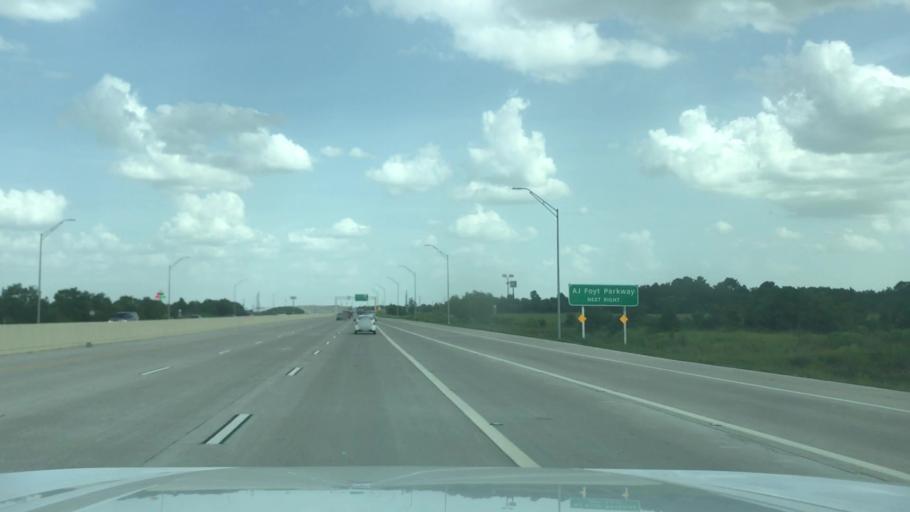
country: US
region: Texas
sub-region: Waller County
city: Waller
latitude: 30.0670
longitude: -95.9174
